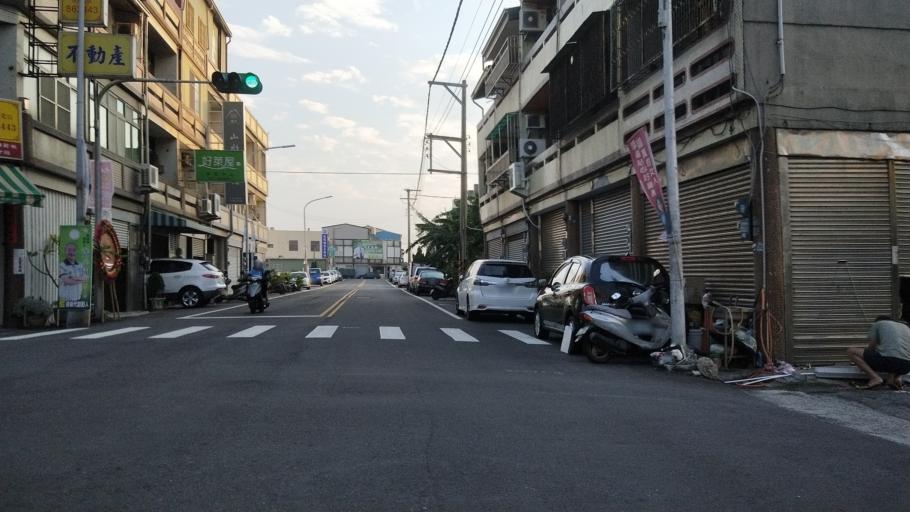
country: TW
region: Taiwan
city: Fengyuan
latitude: 24.4384
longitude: 120.6529
